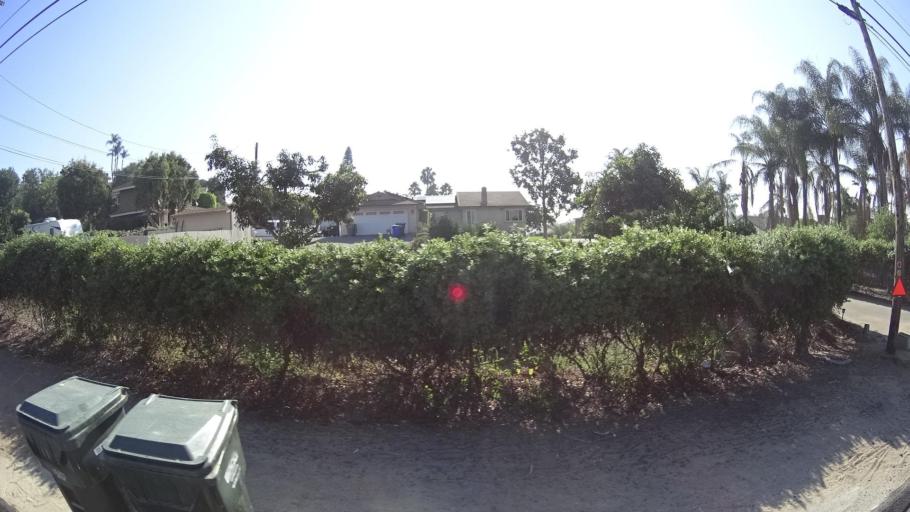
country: US
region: California
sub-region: San Diego County
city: Fallbrook
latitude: 33.3383
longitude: -117.2449
